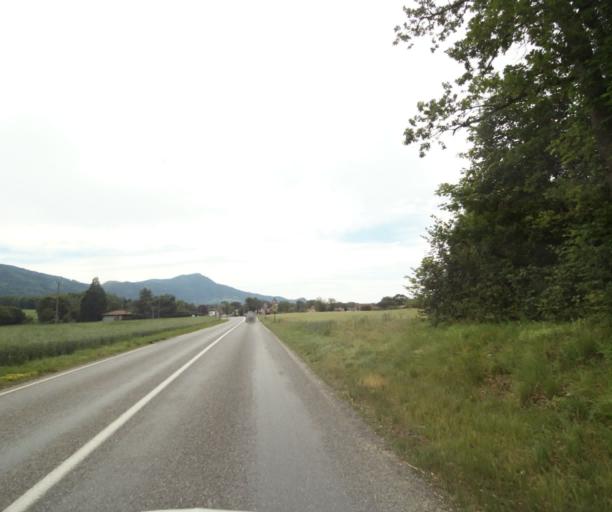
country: FR
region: Rhone-Alpes
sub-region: Departement de la Haute-Savoie
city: Perrignier
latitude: 46.2970
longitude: 6.4310
